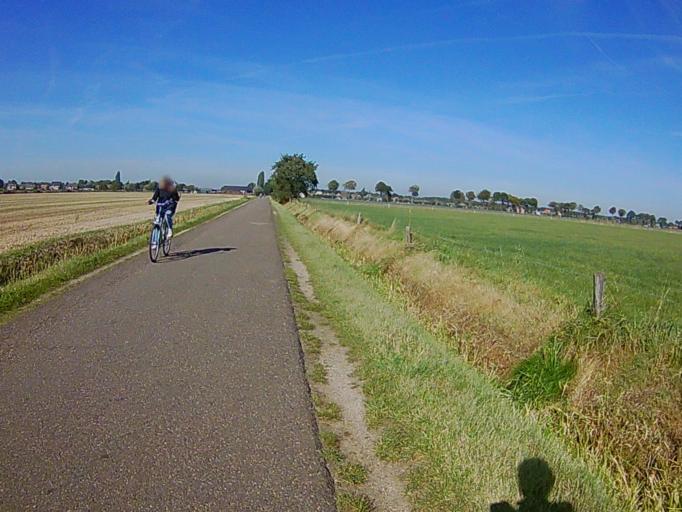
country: BE
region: Flanders
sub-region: Provincie Antwerpen
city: Stabroek
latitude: 51.3258
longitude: 4.3966
